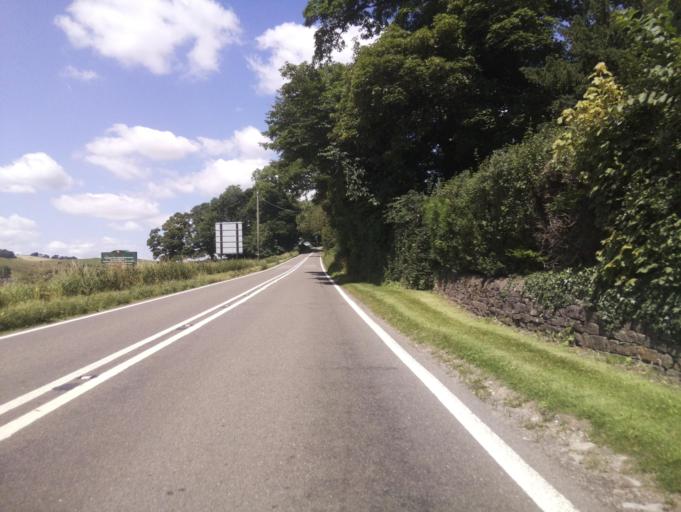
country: GB
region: England
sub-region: Derbyshire
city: Ashbourne
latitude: 53.0634
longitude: -1.7464
